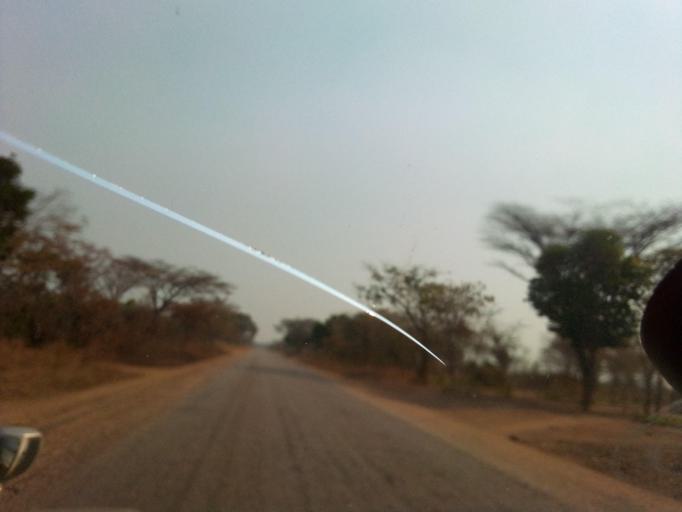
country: ZM
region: Northern
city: Chinsali
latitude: -10.7720
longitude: 32.0463
